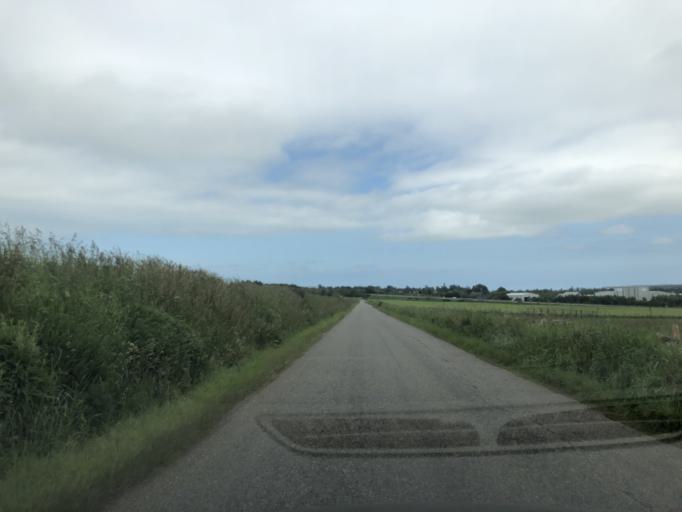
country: GB
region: Scotland
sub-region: Angus
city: Brechin
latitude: 56.7363
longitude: -2.6948
